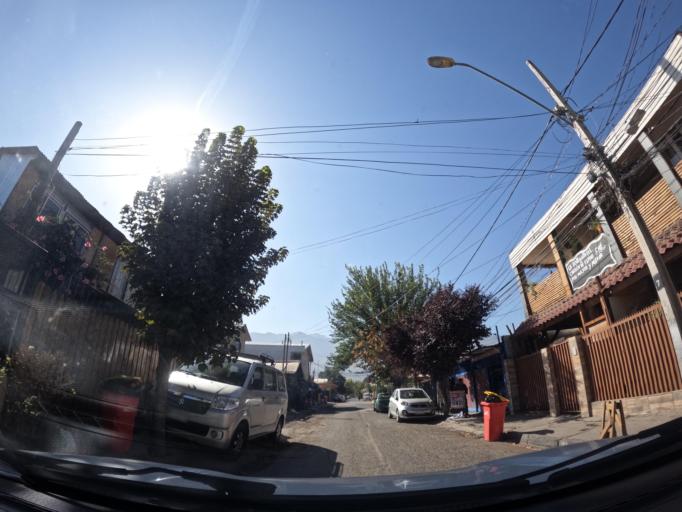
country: CL
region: Santiago Metropolitan
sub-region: Provincia de Santiago
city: Villa Presidente Frei, Nunoa, Santiago, Chile
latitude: -33.4634
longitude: -70.5636
